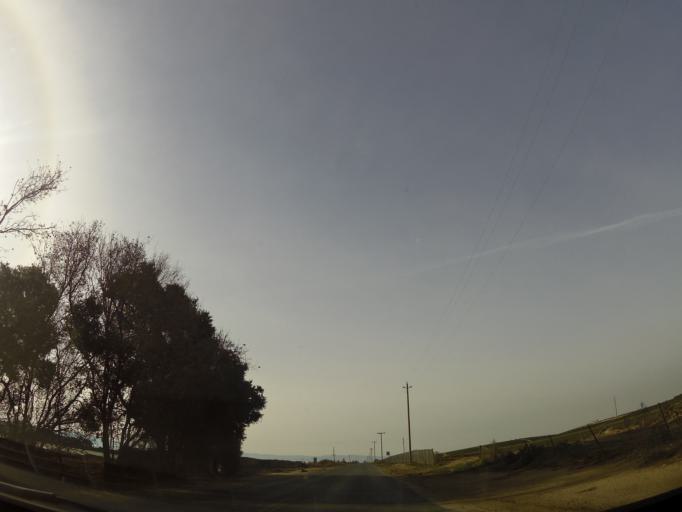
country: US
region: California
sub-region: Monterey County
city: Prunedale
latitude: 36.7712
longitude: -121.6056
